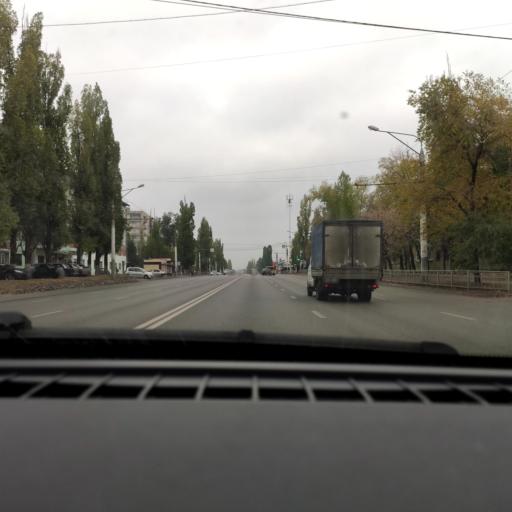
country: RU
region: Voronezj
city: Maslovka
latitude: 51.6085
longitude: 39.2373
